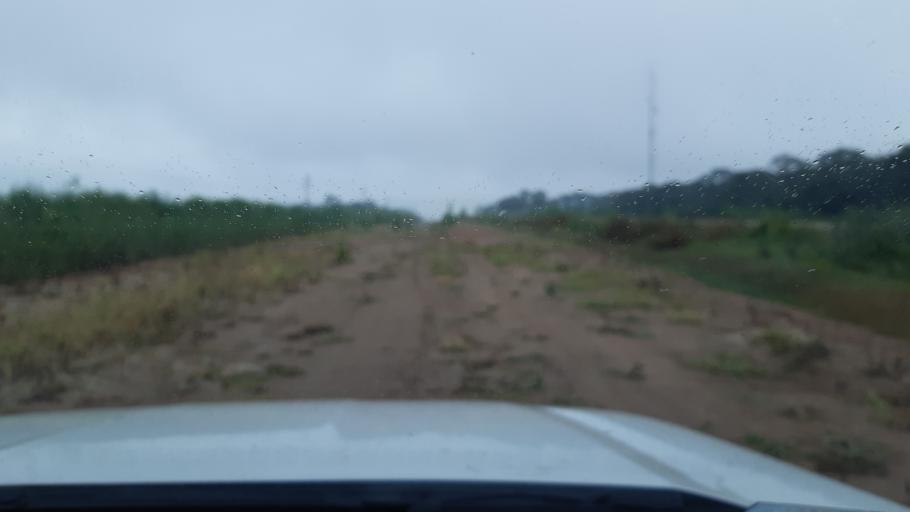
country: AR
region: Jujuy
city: La Mendieta
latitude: -24.3756
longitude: -65.0090
